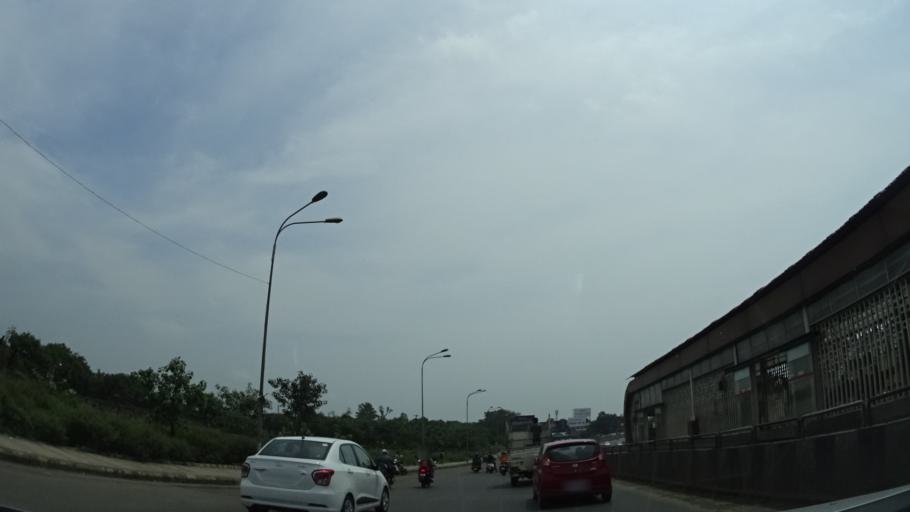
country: IN
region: Maharashtra
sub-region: Pune Division
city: Lohogaon
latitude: 18.5634
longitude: 73.9329
